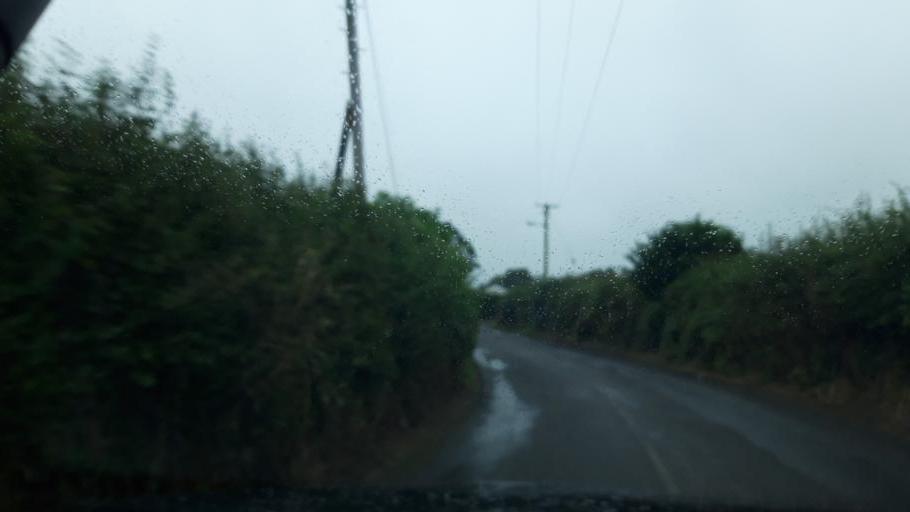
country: IE
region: Leinster
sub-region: Kilkenny
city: Callan
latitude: 52.6288
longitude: -7.5484
